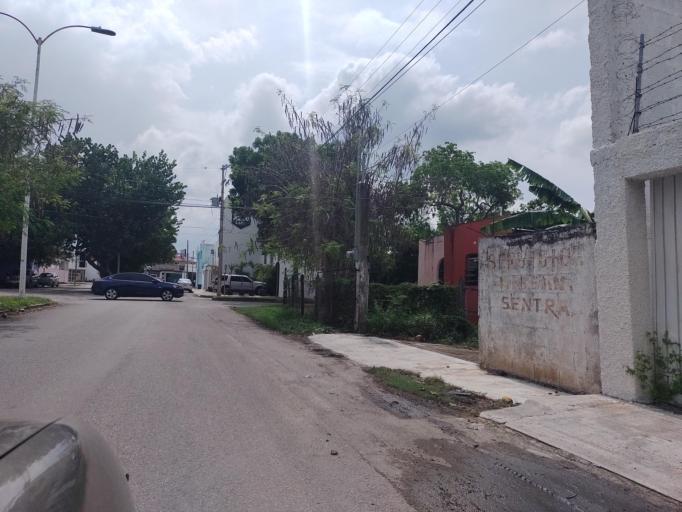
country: MX
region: Quintana Roo
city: Chetumal
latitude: 18.5170
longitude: -88.3137
